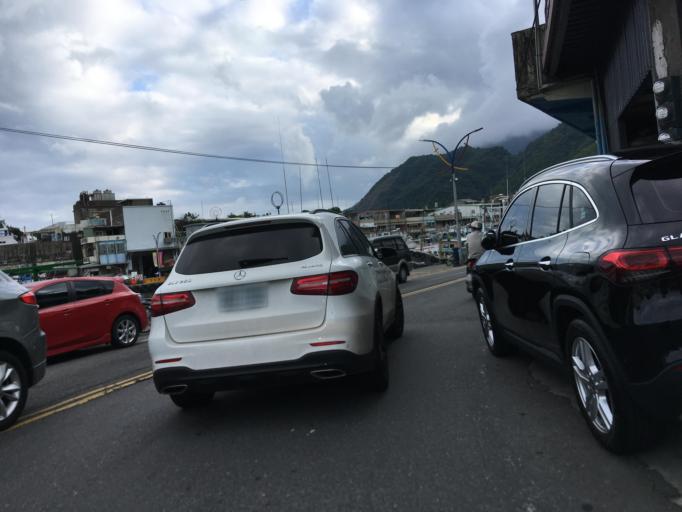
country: TW
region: Taiwan
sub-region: Yilan
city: Yilan
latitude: 24.5798
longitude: 121.8707
